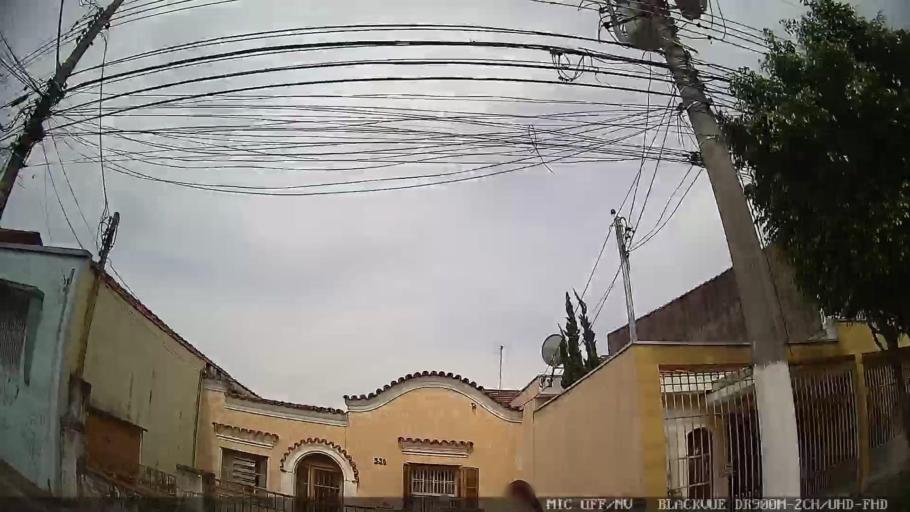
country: BR
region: Sao Paulo
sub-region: Guarulhos
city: Guarulhos
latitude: -23.5292
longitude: -46.5452
